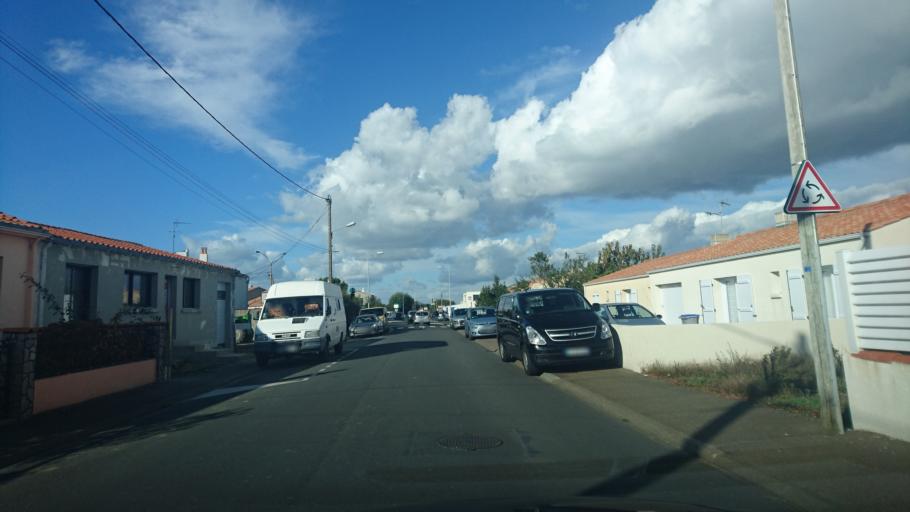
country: FR
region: Pays de la Loire
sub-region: Departement de la Vendee
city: Les Sables-d'Olonne
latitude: 46.5083
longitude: -1.8025
